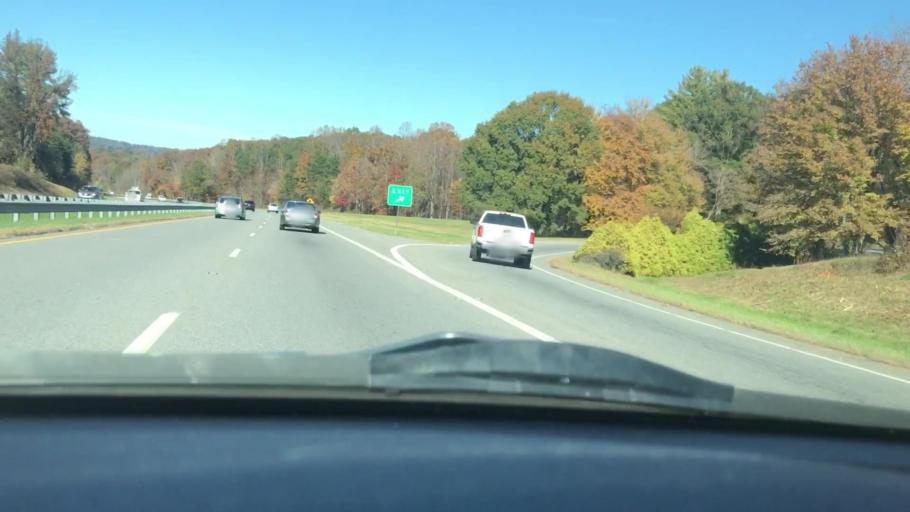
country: US
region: North Carolina
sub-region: Rockingham County
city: Madison
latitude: 36.3752
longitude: -79.9420
